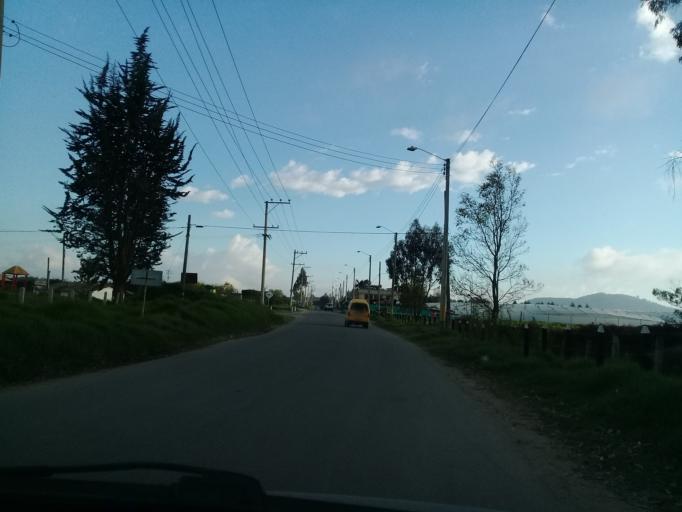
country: CO
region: Cundinamarca
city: Madrid
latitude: 4.7589
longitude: -74.2641
